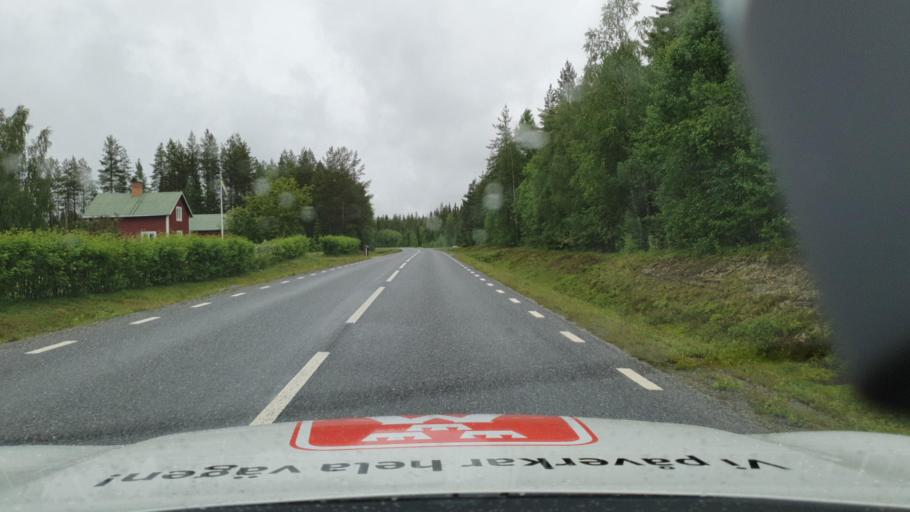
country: SE
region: Vaesterbotten
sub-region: Asele Kommun
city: Asele
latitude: 63.9802
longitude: 17.2640
